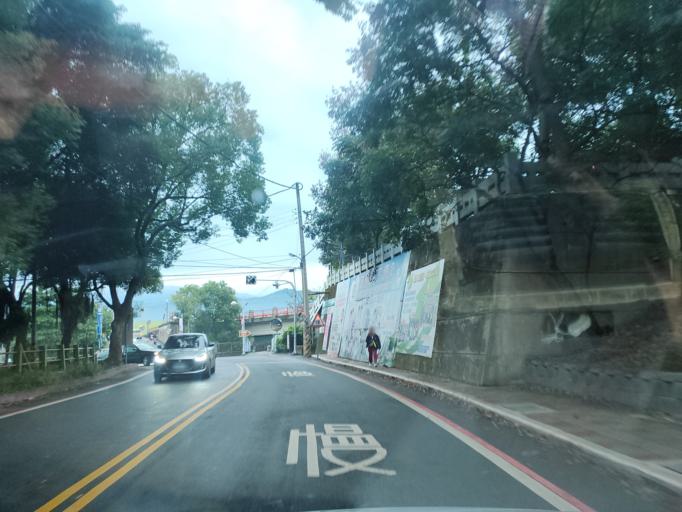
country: TW
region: Taiwan
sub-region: Miaoli
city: Miaoli
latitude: 24.5565
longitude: 120.8131
